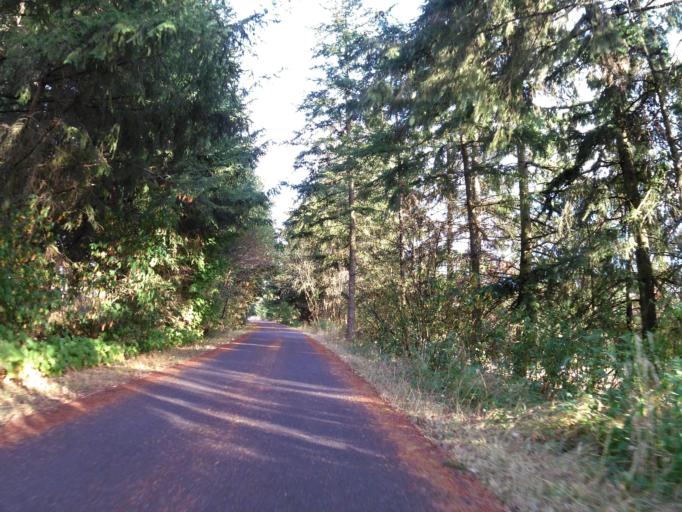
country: US
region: Washington
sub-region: Thurston County
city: Rainier
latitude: 46.8762
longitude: -122.7292
